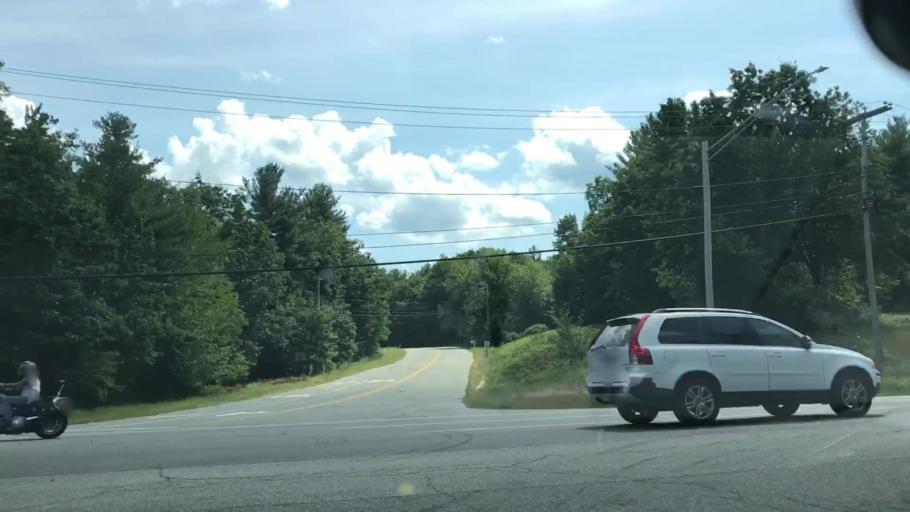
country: US
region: New Hampshire
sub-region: Hillsborough County
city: Bedford
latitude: 42.9100
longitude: -71.5649
